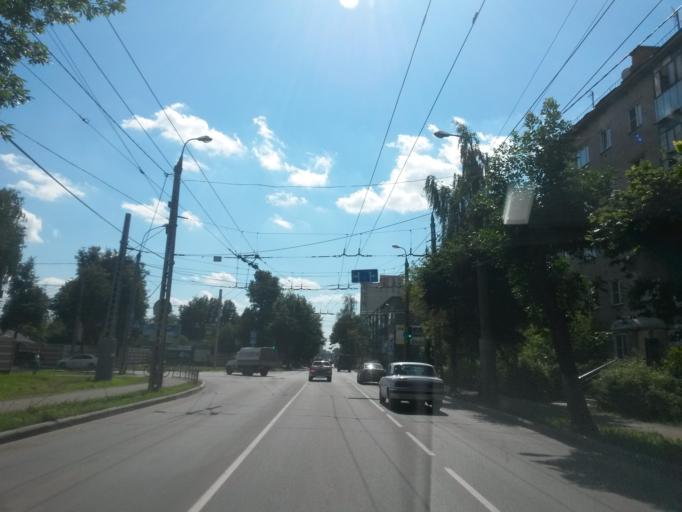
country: RU
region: Ivanovo
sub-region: Gorod Ivanovo
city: Ivanovo
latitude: 56.9882
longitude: 40.9836
